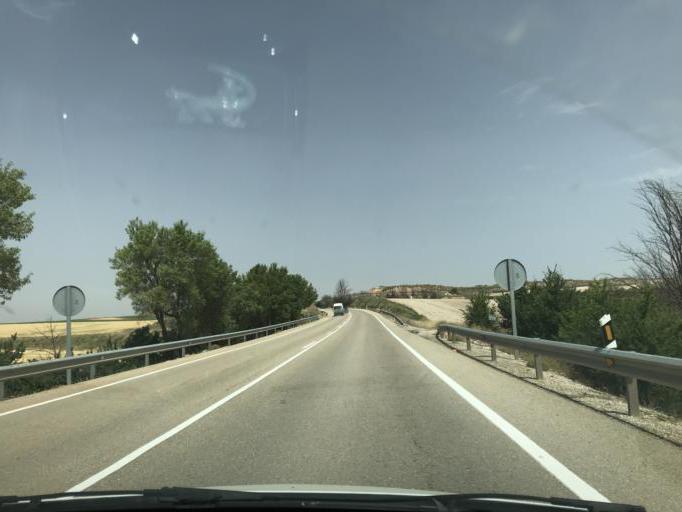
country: ES
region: Castille-La Mancha
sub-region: Provincia de Cuenca
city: Villar de Domingo Garcia
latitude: 40.2523
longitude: -2.3094
